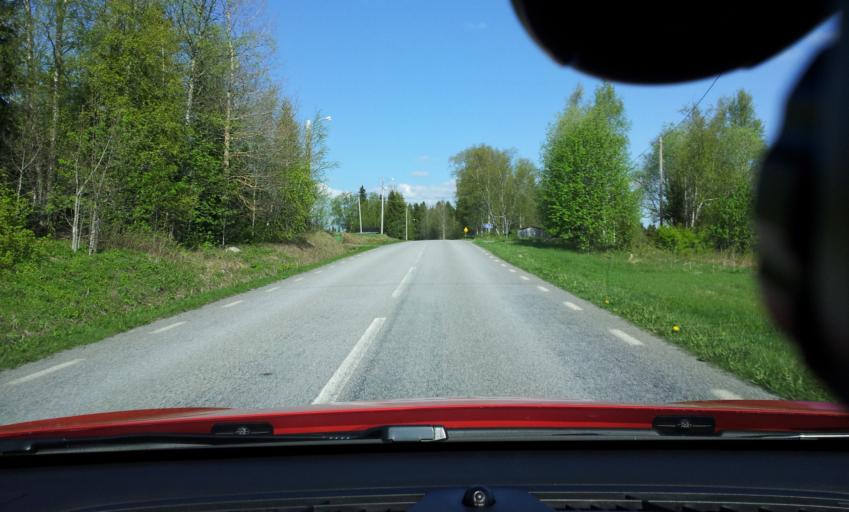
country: SE
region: Jaemtland
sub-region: Krokoms Kommun
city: Krokom
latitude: 63.1488
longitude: 14.1671
